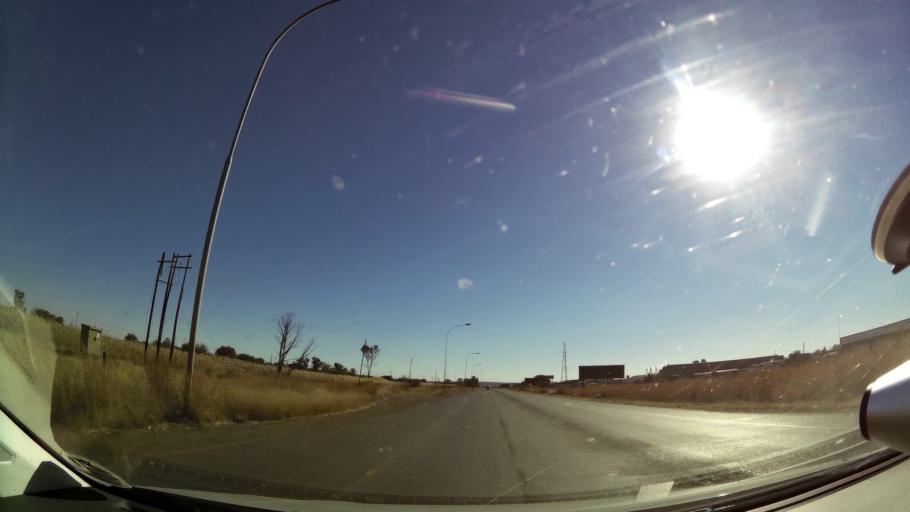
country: ZA
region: Northern Cape
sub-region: Frances Baard District Municipality
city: Kimberley
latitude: -28.7048
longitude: 24.7769
